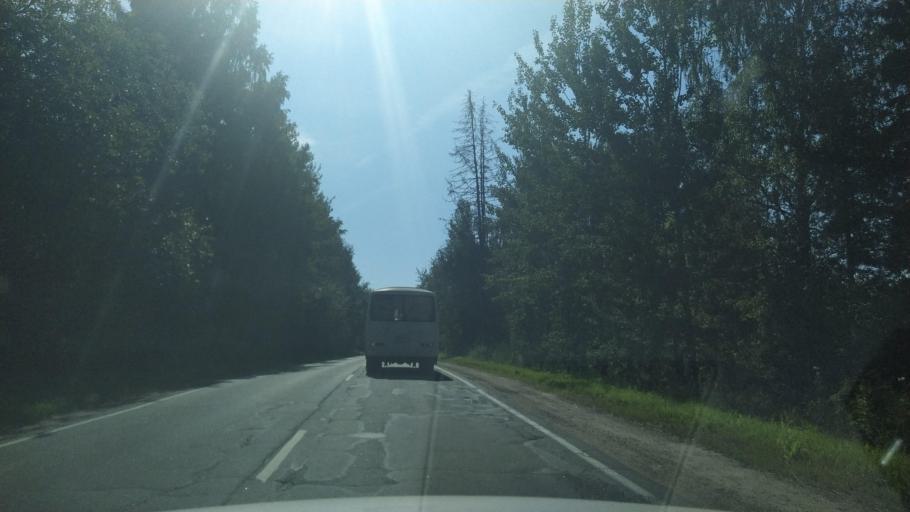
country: RU
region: Leningrad
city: Siverskiy
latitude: 59.3327
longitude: 30.0589
